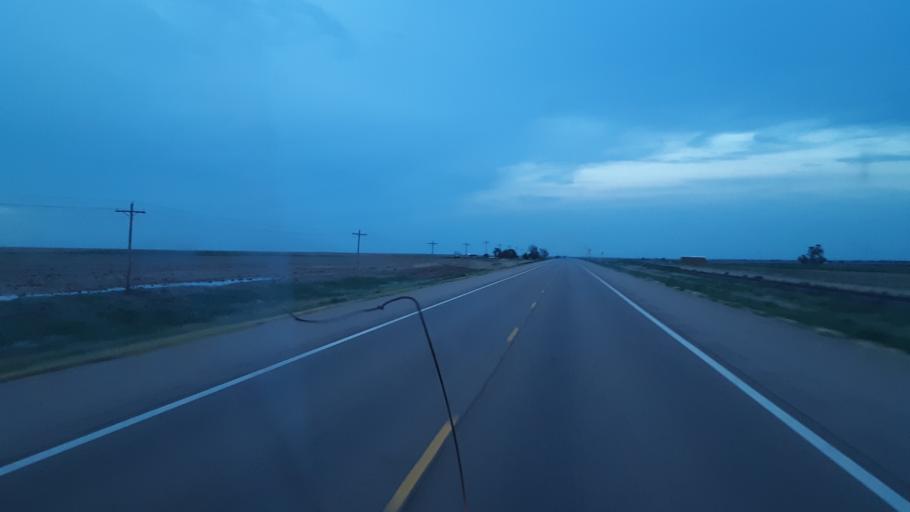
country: US
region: Kansas
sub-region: Hamilton County
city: Syracuse
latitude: 37.9628
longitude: -101.6757
